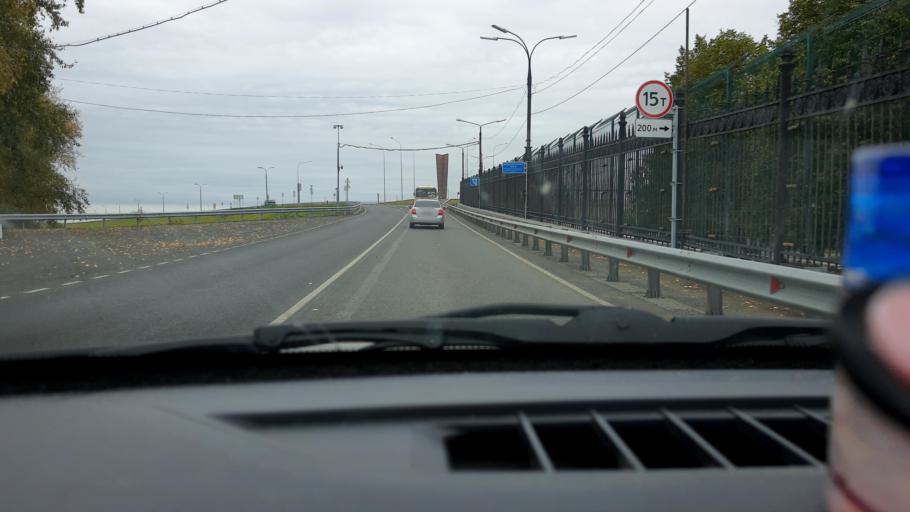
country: RU
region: Nizjnij Novgorod
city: Zavolzh'ye
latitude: 56.6475
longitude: 43.3772
